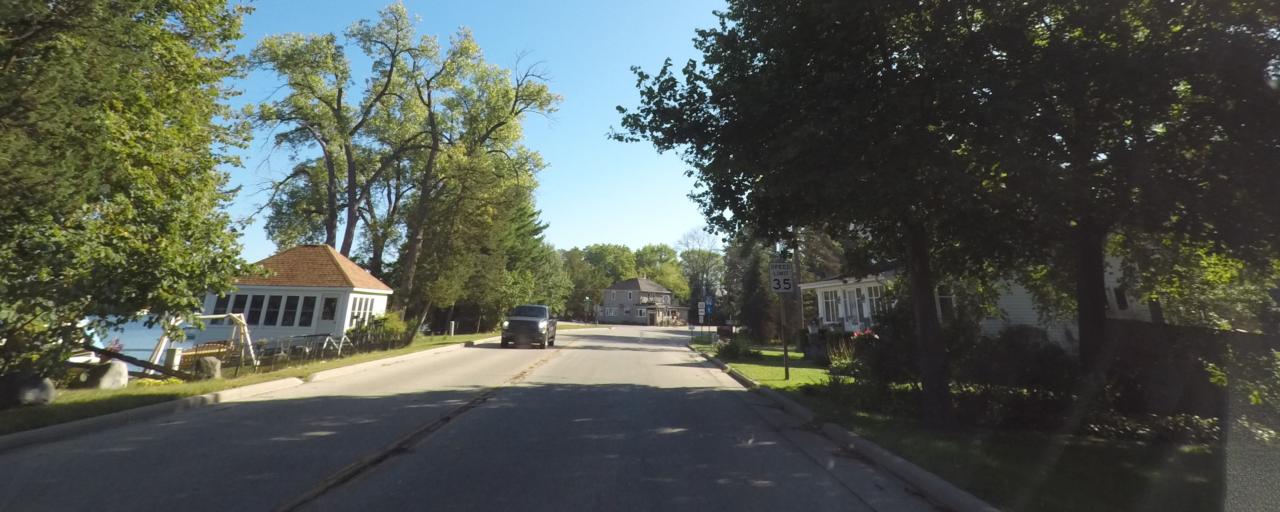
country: US
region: Wisconsin
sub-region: Waukesha County
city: Dousman
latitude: 43.0273
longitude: -88.5316
